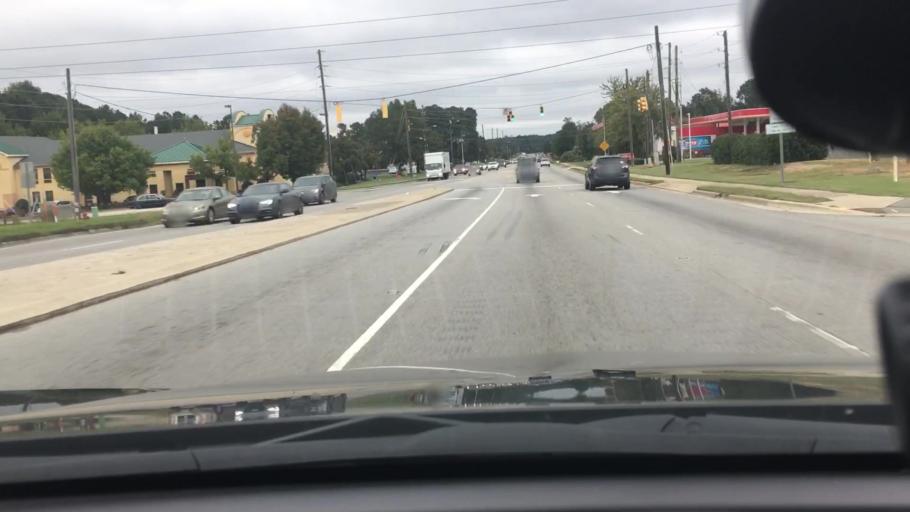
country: US
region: North Carolina
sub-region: Wake County
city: Apex
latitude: 35.7128
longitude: -78.8395
